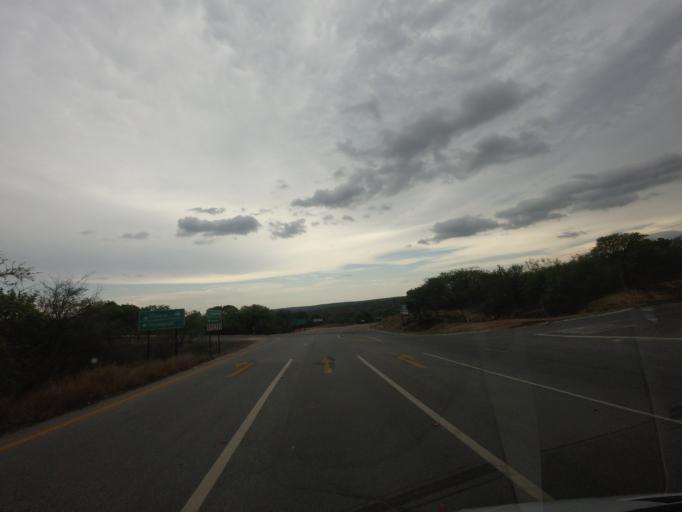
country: ZA
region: Limpopo
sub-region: Mopani District Municipality
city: Hoedspruit
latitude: -24.5402
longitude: 31.0306
